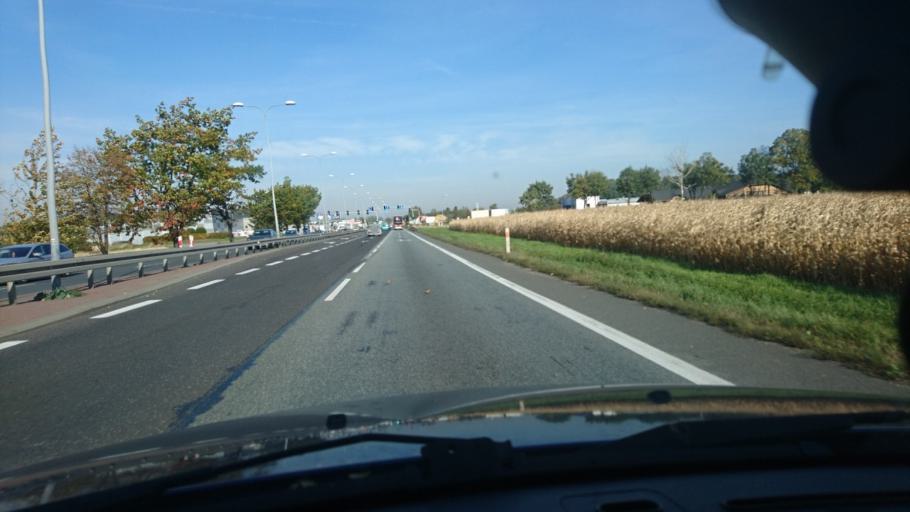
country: PL
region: Silesian Voivodeship
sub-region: Powiat pszczynski
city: Goczalkowice Zdroj
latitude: 49.9545
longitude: 18.9664
